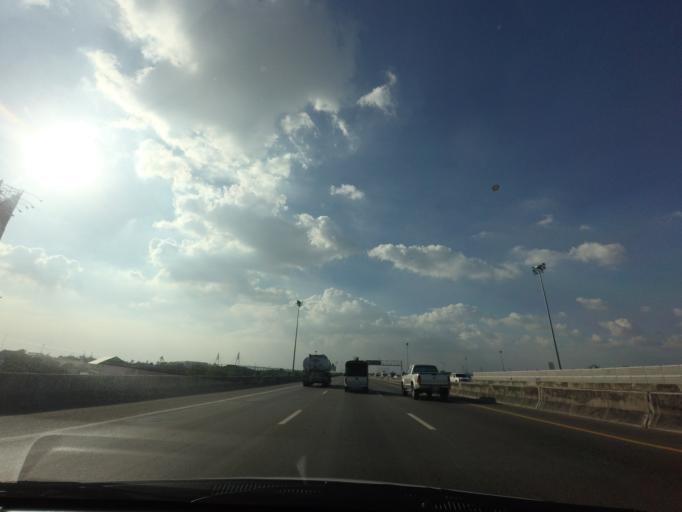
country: TH
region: Samut Prakan
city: Phra Samut Chedi
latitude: 13.6340
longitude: 100.5692
